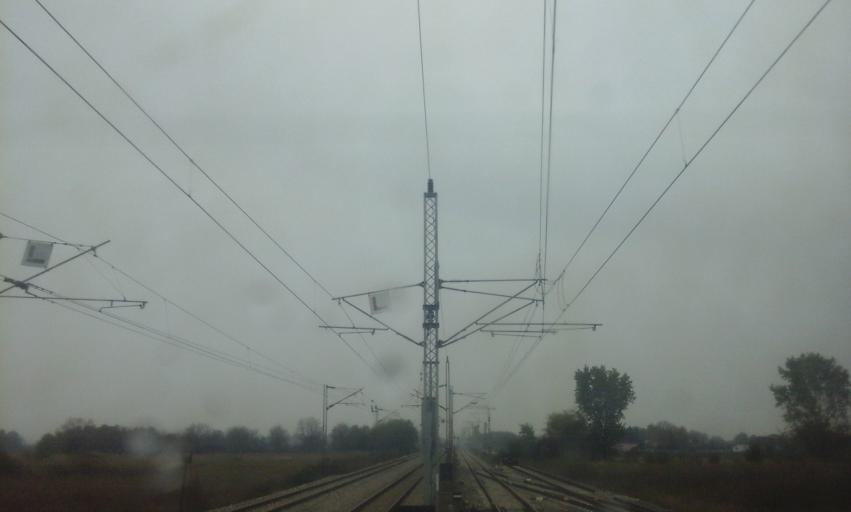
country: RS
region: Central Serbia
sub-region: Pomoravski Okrug
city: Paracin
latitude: 43.8718
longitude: 21.3938
